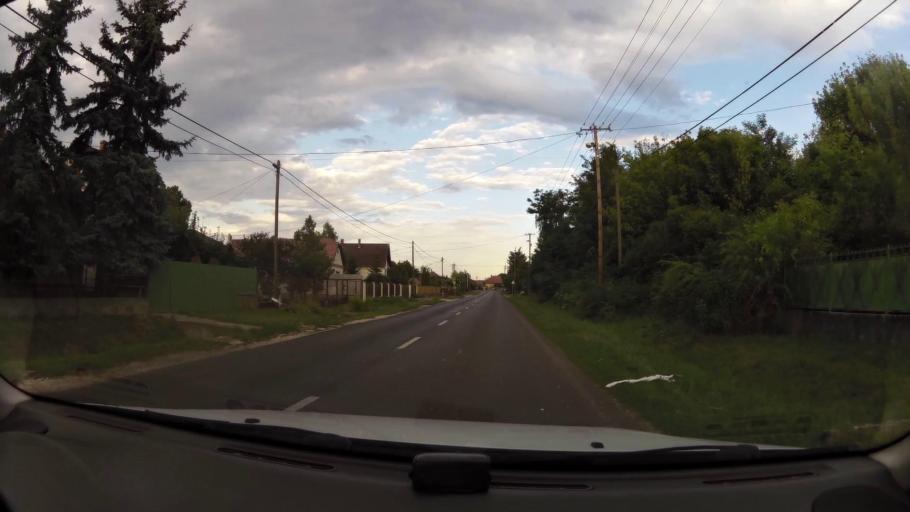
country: HU
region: Pest
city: Tapiobicske
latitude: 47.3661
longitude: 19.6870
